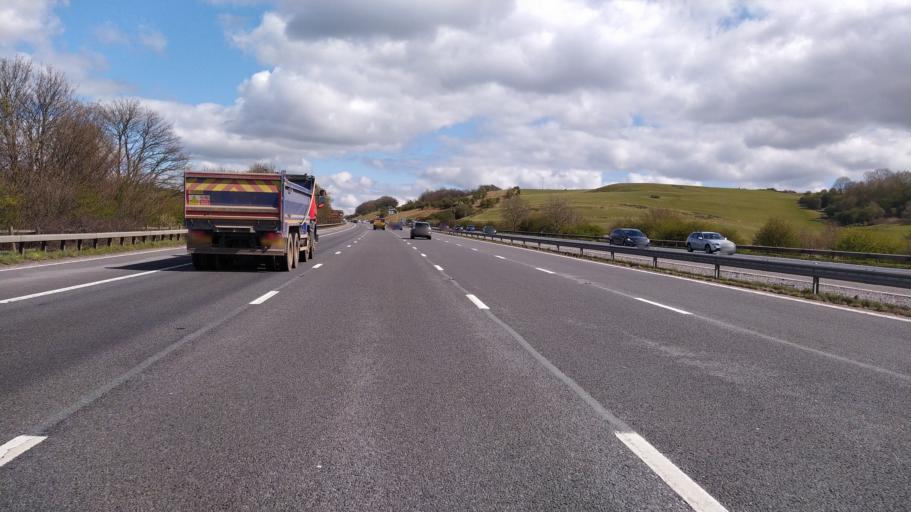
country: GB
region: England
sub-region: South Gloucestershire
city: Hinton
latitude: 51.4990
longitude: -2.3763
